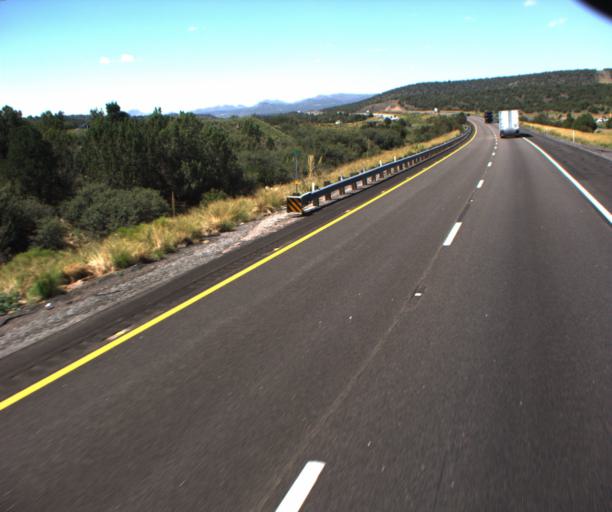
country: US
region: Arizona
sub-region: Mohave County
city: Peach Springs
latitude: 35.2071
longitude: -113.2949
